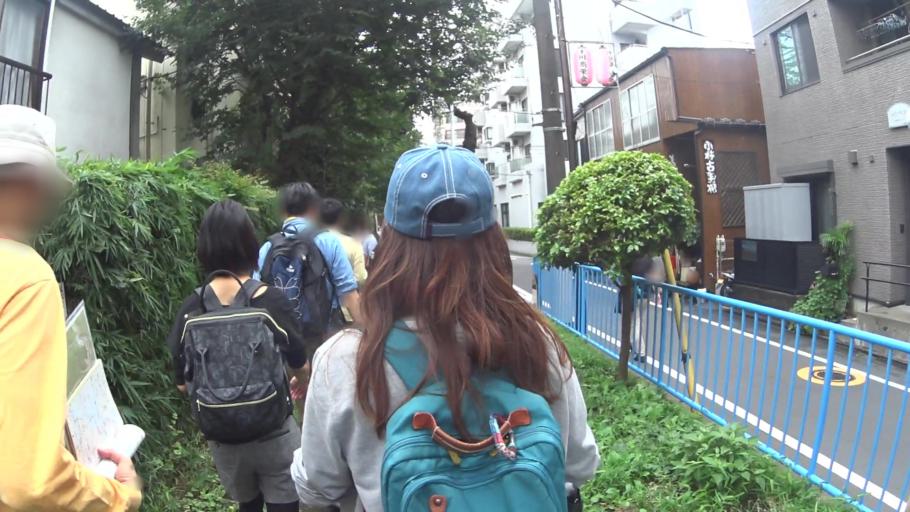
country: JP
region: Tokyo
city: Tokyo
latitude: 35.7376
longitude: 139.6863
